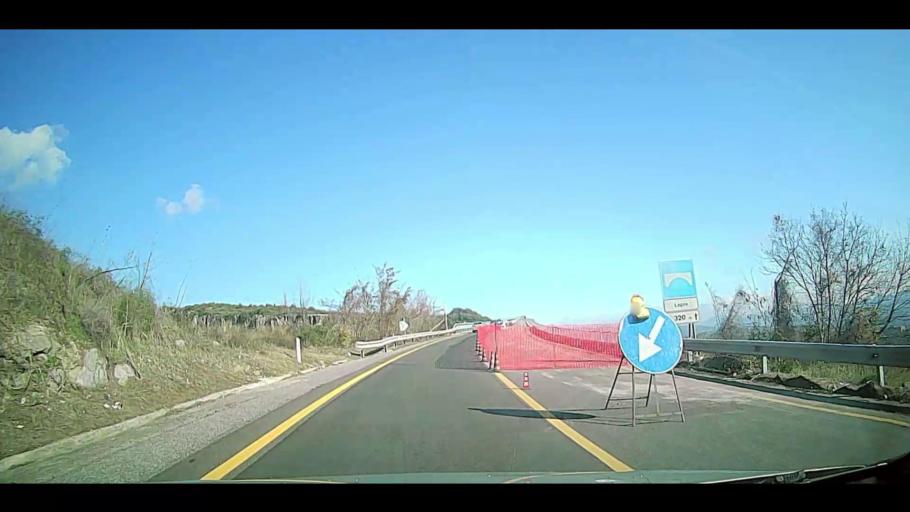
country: IT
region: Calabria
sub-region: Provincia di Crotone
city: Caccuri
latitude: 39.2225
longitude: 16.7936
